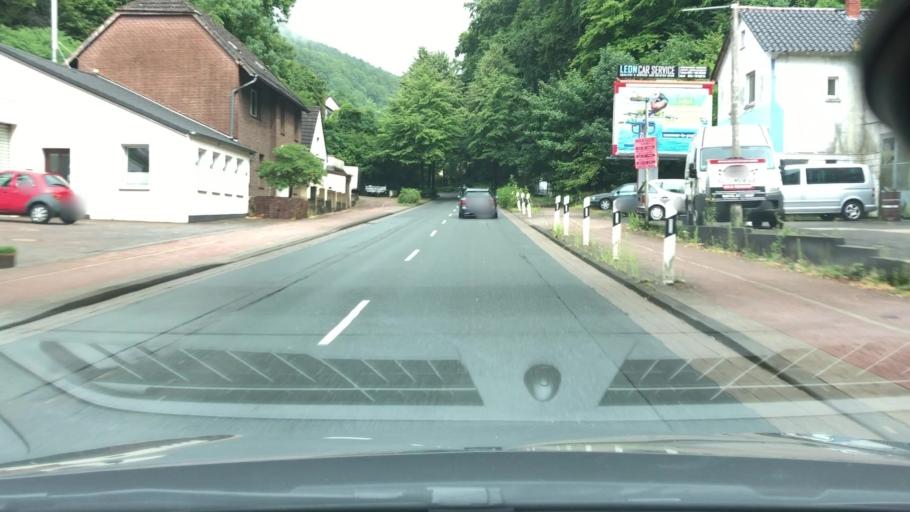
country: DE
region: North Rhine-Westphalia
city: Porta Westfalica
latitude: 52.2394
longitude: 8.9260
